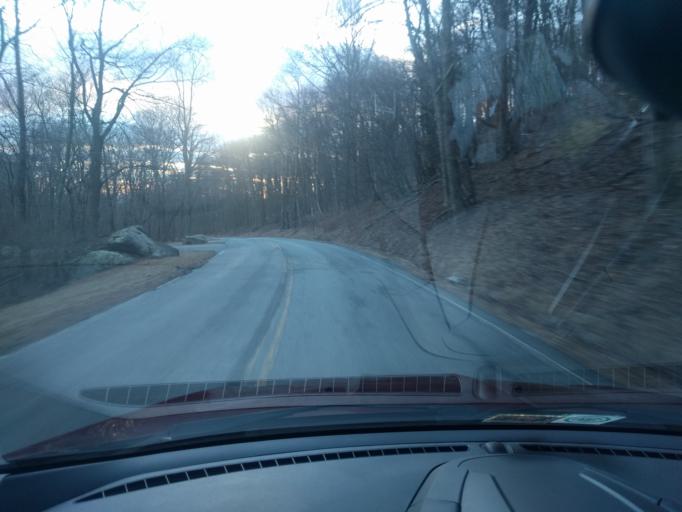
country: US
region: Virginia
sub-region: Botetourt County
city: Buchanan
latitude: 37.4416
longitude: -79.5983
